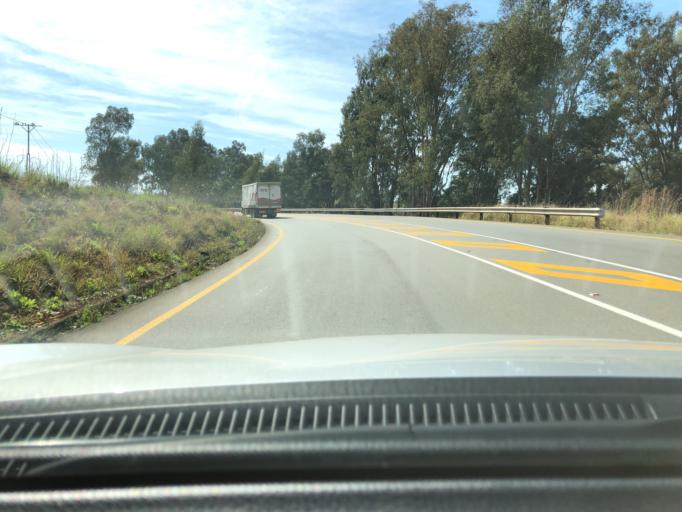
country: ZA
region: KwaZulu-Natal
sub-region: Sisonke District Municipality
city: Ixopo
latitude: -30.0575
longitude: 30.1874
